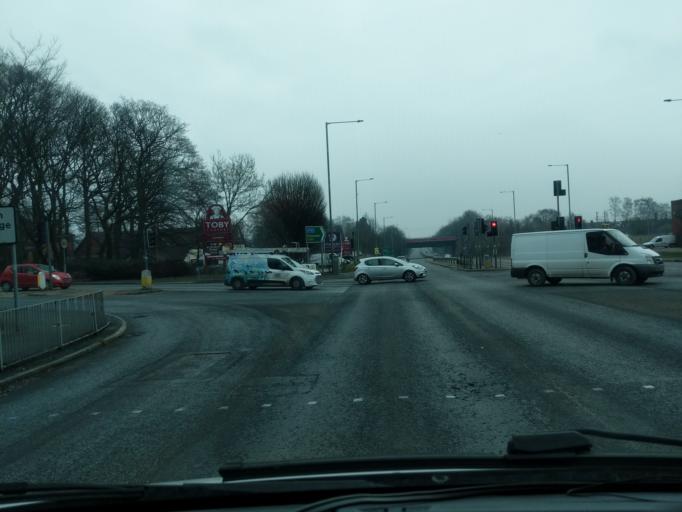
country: GB
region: England
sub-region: St. Helens
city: St Helens
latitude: 53.4727
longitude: -2.7194
